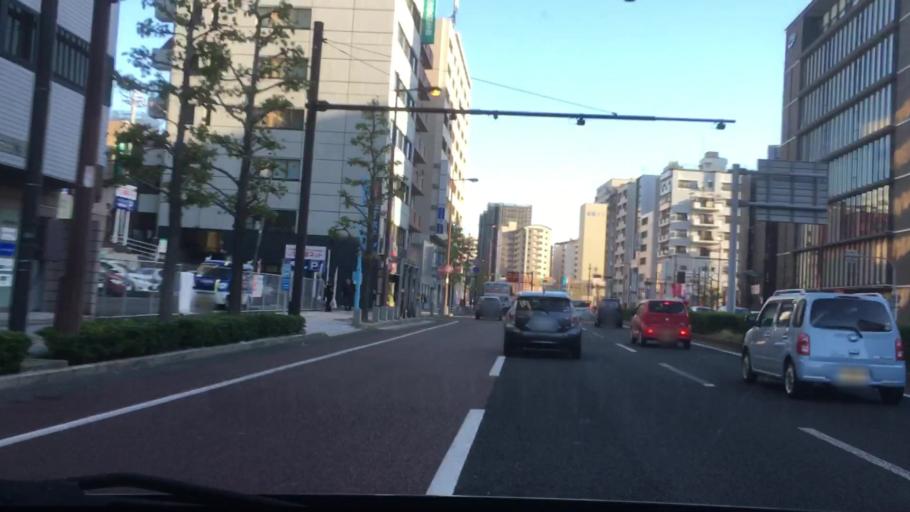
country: JP
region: Nagasaki
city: Sasebo
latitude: 33.1672
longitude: 129.7245
